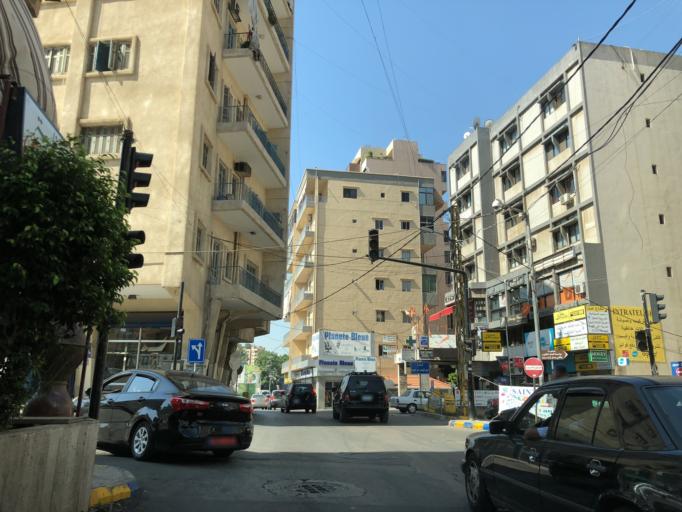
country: LB
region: Mont-Liban
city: Jdaidet el Matn
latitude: 33.8762
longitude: 35.5478
